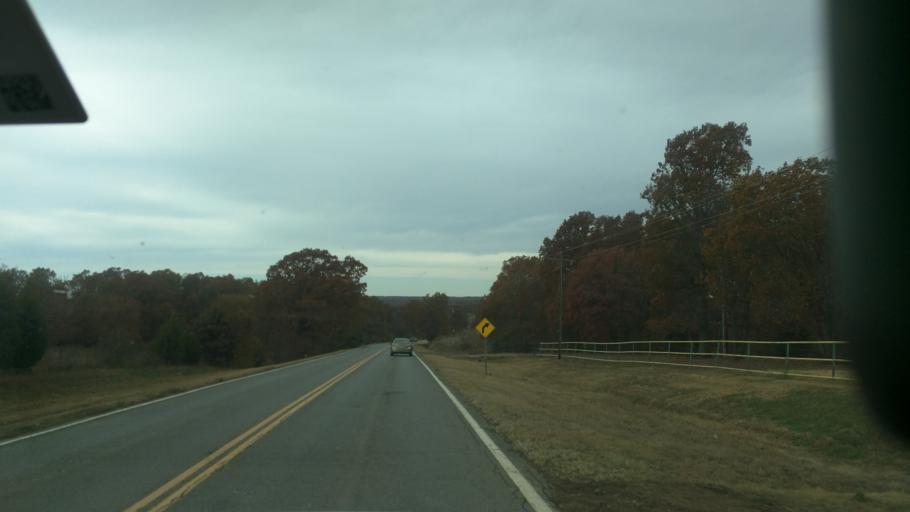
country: US
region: Oklahoma
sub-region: Cherokee County
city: Park Hill
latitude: 35.9030
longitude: -94.8221
